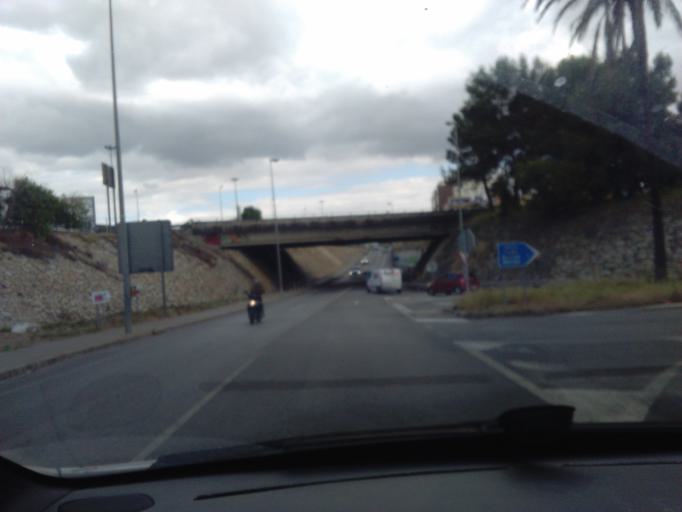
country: ES
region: Andalusia
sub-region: Provincia de Sevilla
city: Sevilla
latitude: 37.3832
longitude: -5.9428
